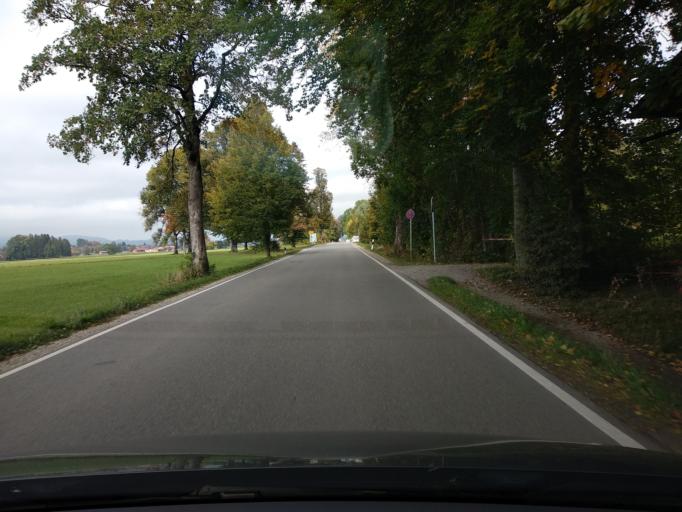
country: DE
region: Bavaria
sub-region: Swabia
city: Schwangau
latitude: 47.5615
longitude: 10.7421
